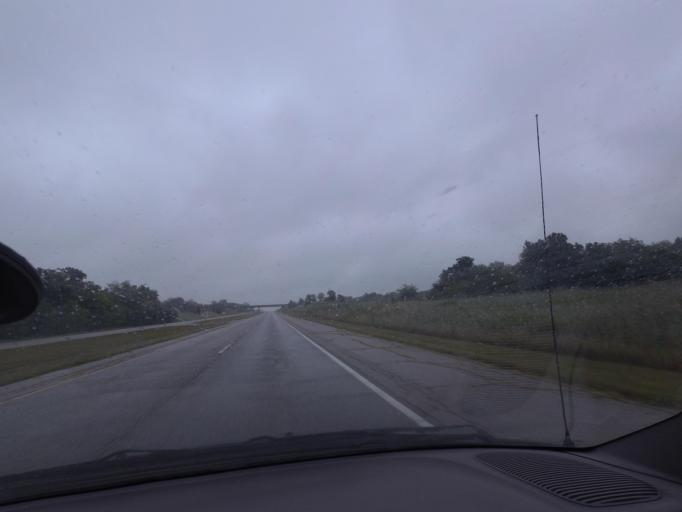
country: US
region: Illinois
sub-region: Pike County
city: Barry
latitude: 39.6899
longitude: -90.9201
